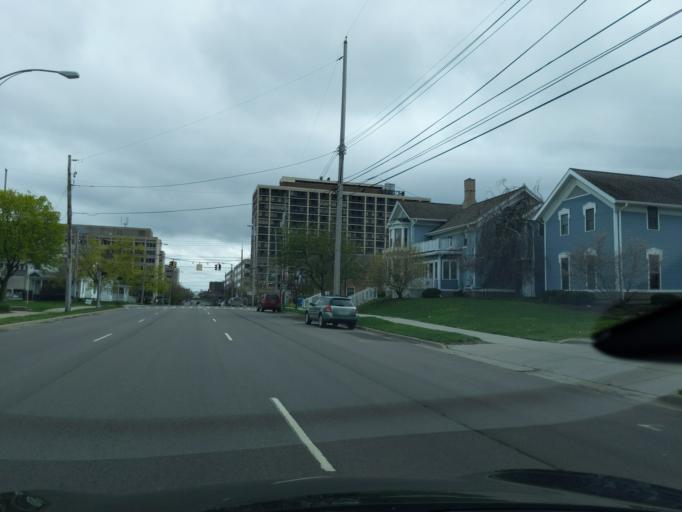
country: US
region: Michigan
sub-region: Ingham County
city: Lansing
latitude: 42.7366
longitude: -84.5601
